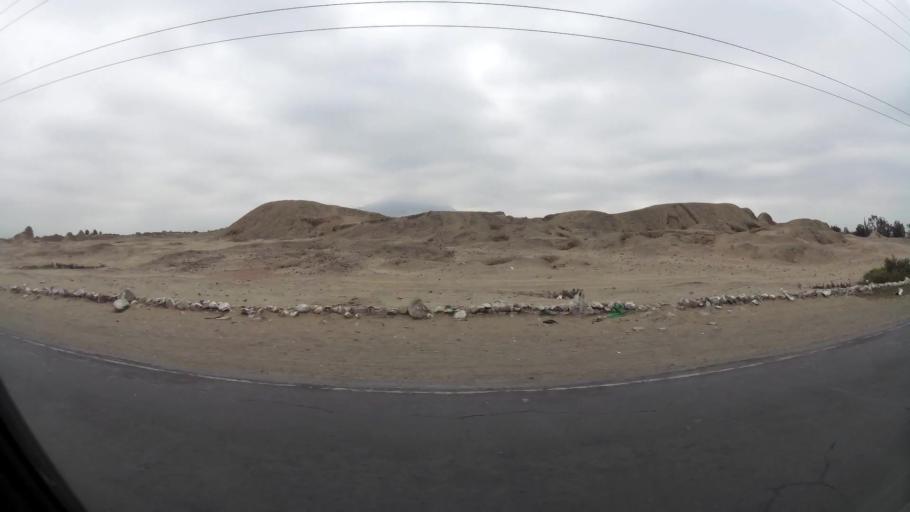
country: PE
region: La Libertad
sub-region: Provincia de Trujillo
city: La Esperanza
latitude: -8.0982
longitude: -79.0686
